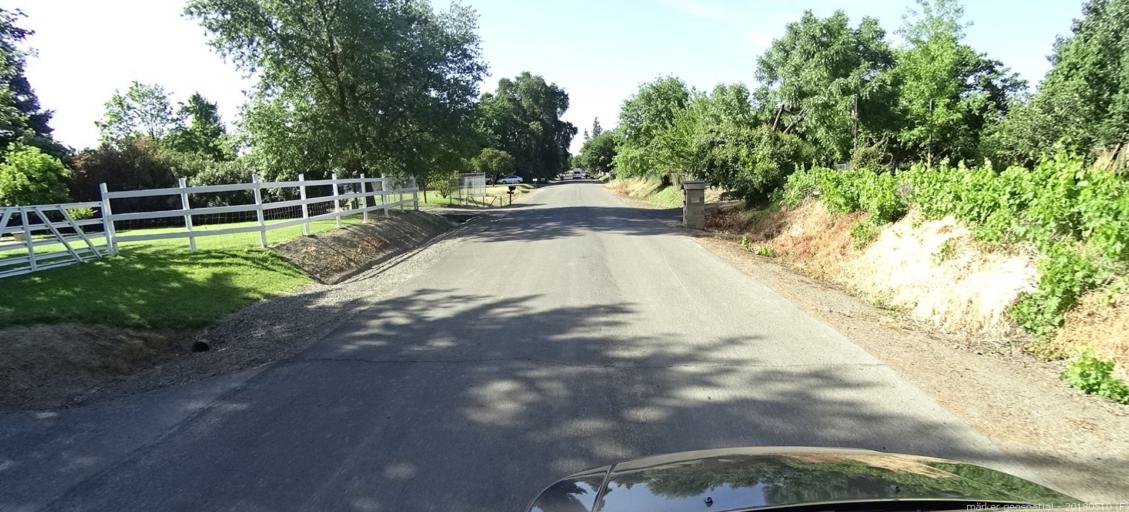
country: US
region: California
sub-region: Sacramento County
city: Rio Linda
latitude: 38.6613
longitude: -121.4786
